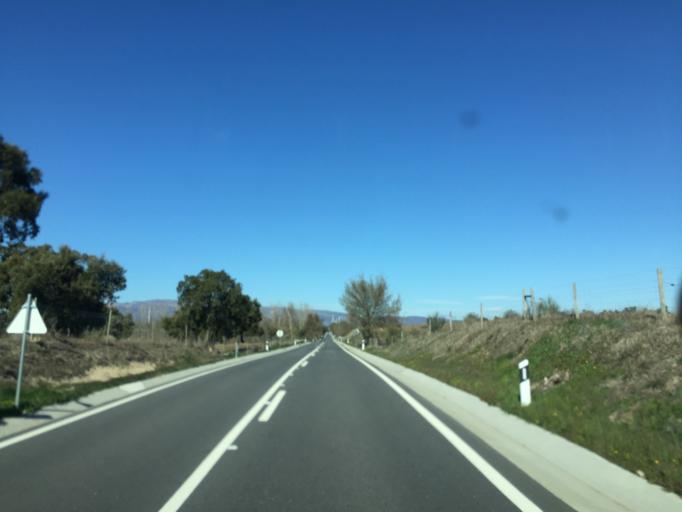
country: PT
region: Guarda
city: Alcains
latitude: 39.9661
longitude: -7.4537
